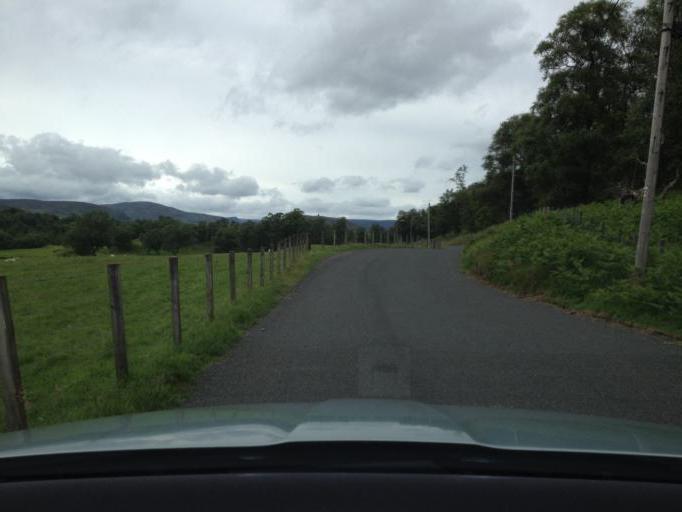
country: GB
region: Scotland
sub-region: Aberdeenshire
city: Aboyne
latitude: 56.8973
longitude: -2.8023
